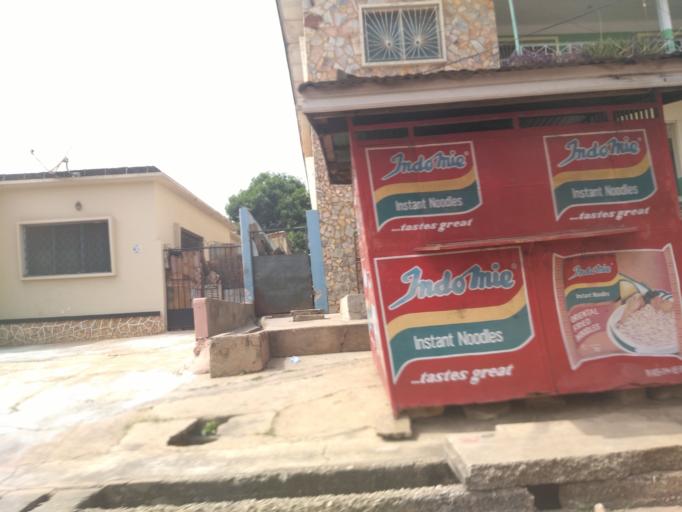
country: GH
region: Ashanti
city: Kumasi
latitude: 6.6836
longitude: -1.5972
